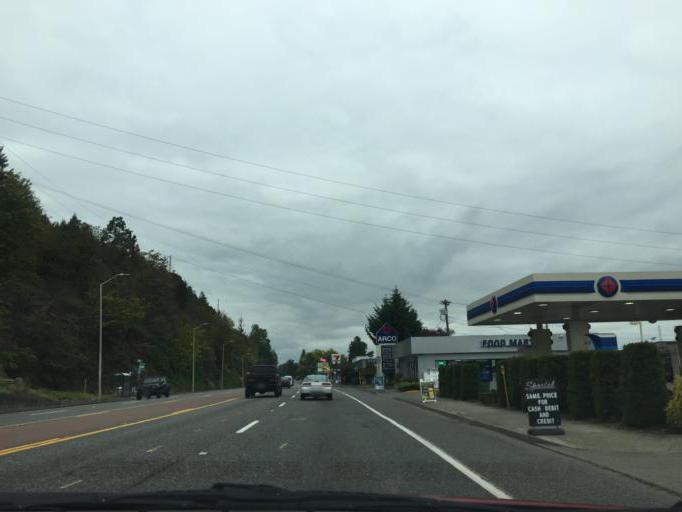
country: US
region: Oregon
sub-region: Washington County
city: Cedar Mill
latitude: 45.6012
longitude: -122.7875
